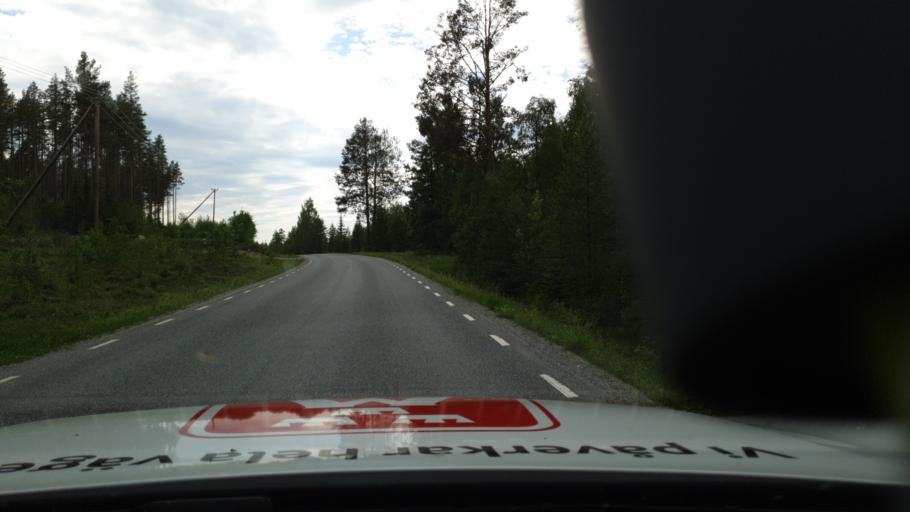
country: SE
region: Jaemtland
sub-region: Braecke Kommun
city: Braecke
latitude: 63.1342
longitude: 15.5121
